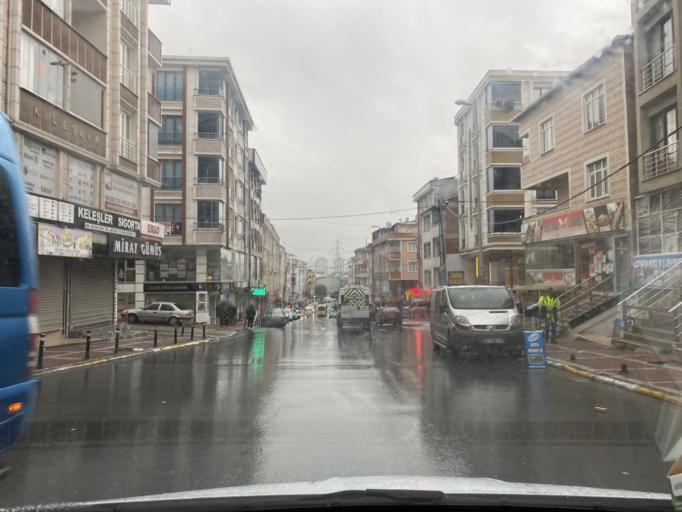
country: TR
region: Istanbul
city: Esenyurt
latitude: 41.0212
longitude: 28.6648
